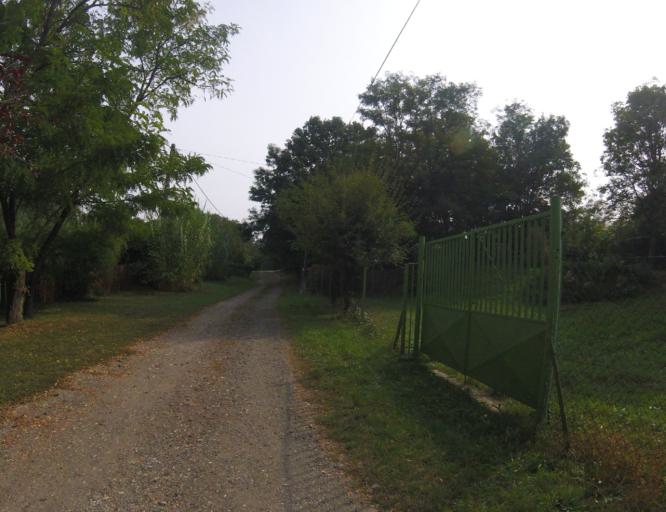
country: HU
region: Pest
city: Veroce
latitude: 47.8364
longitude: 19.0523
